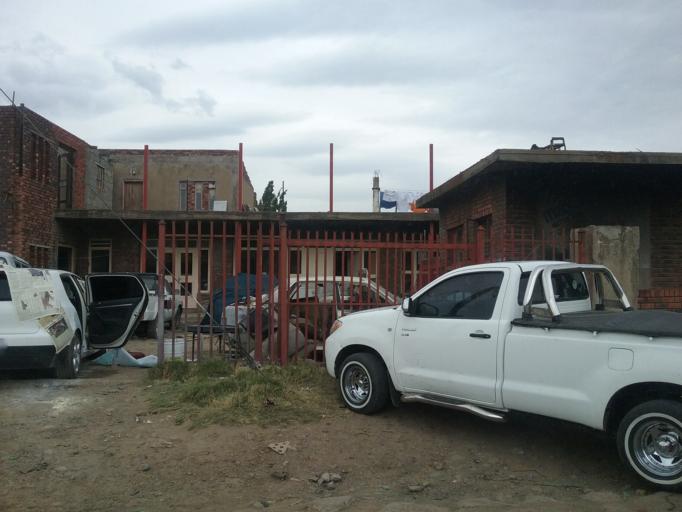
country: LS
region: Maseru
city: Maseru
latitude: -29.3313
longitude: 27.5060
